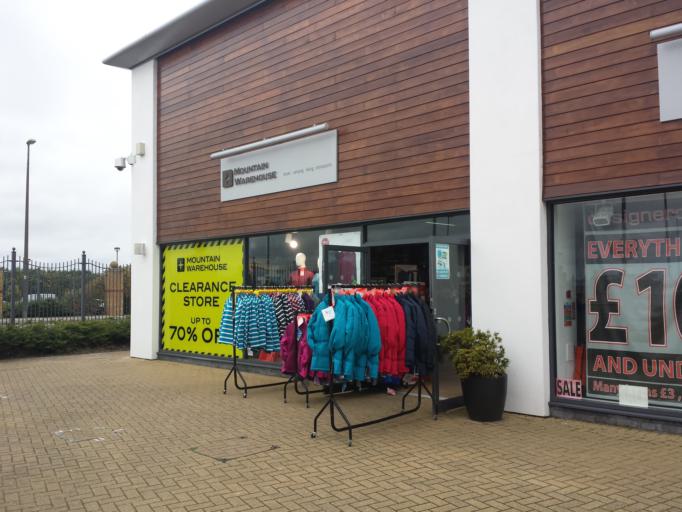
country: GB
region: England
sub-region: Essex
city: Little Clacton
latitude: 51.8183
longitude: 1.1674
